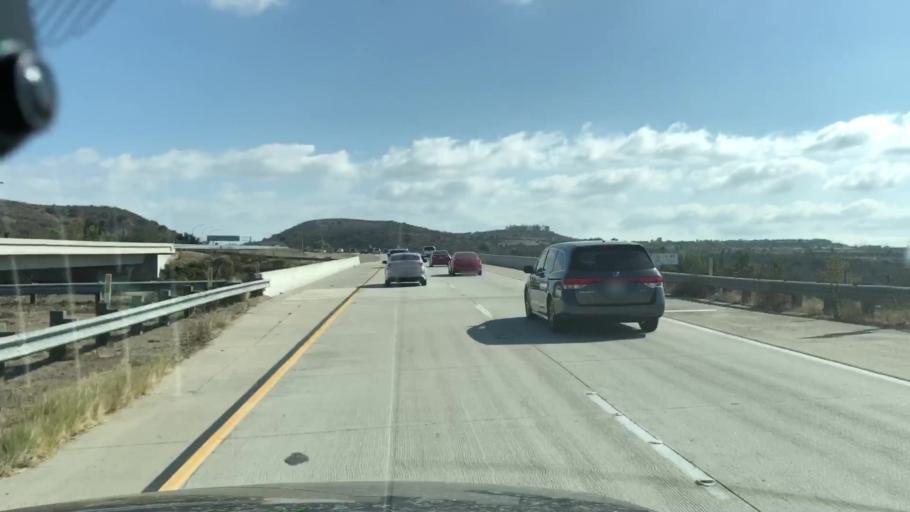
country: US
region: California
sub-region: Ventura County
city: Moorpark
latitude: 34.2826
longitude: -118.8635
